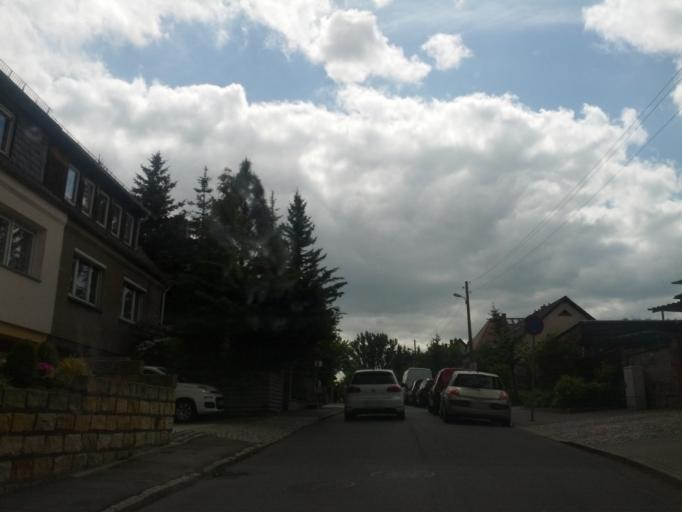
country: DE
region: Saxony
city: Dresden
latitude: 51.0083
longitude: 13.7666
